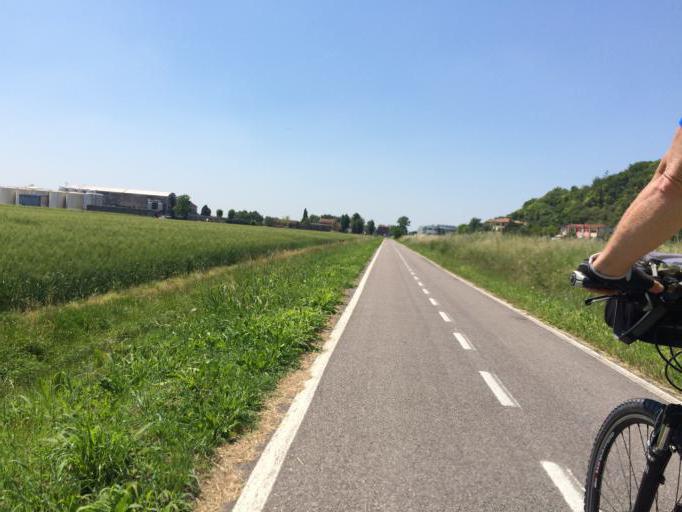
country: IT
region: Veneto
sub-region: Provincia di Vicenza
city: Ponte di Barbarano
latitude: 45.4003
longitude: 11.5702
